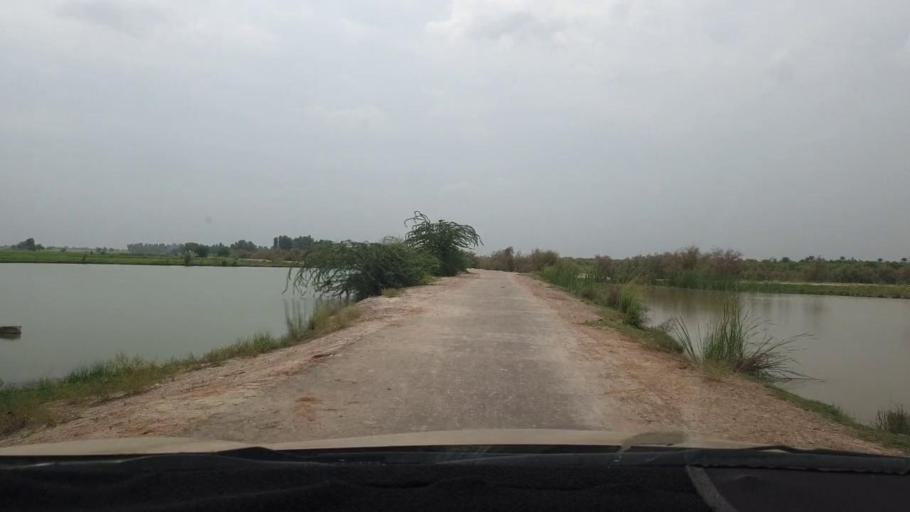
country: PK
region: Sindh
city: Naudero
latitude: 27.6289
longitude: 68.3176
